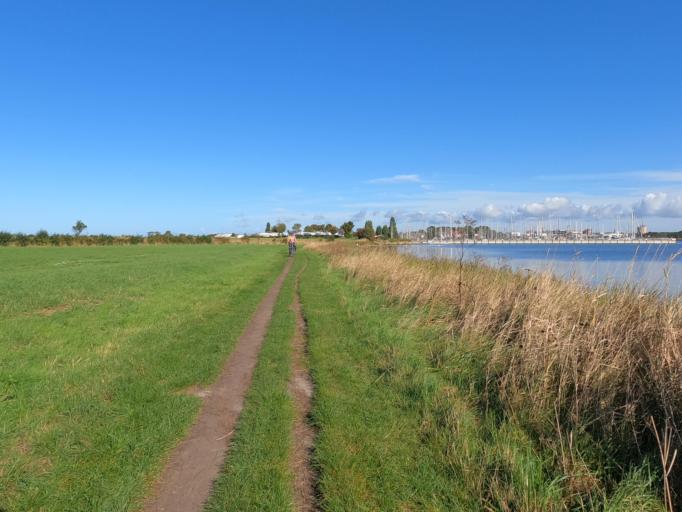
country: DE
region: Schleswig-Holstein
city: Grossenbrode
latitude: 54.3541
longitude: 11.0584
